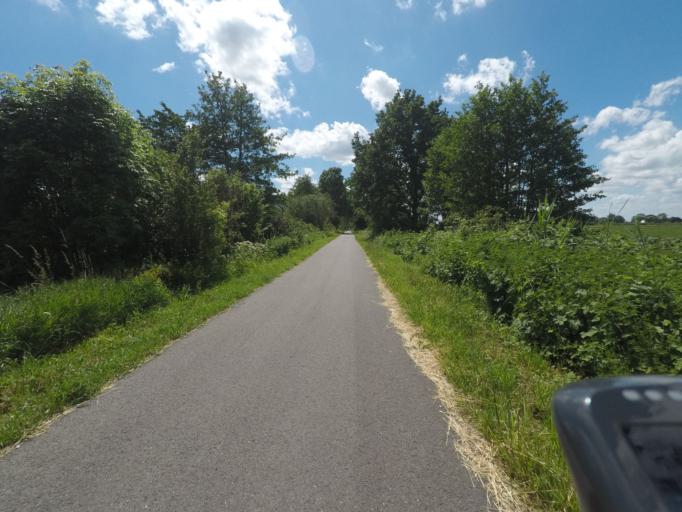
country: DE
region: Hamburg
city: Bergedorf
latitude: 53.4390
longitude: 10.2140
